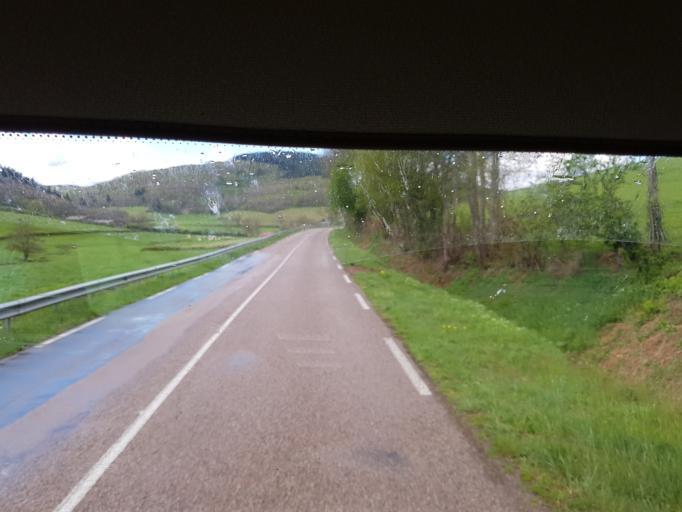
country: FR
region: Bourgogne
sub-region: Departement de Saone-et-Loire
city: Autun
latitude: 47.0646
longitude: 4.2526
